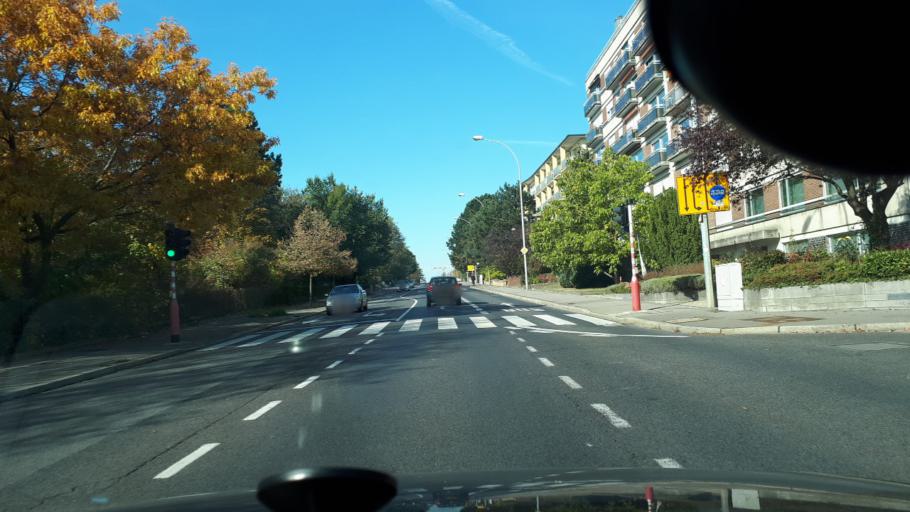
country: LU
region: Luxembourg
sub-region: Canton de Luxembourg
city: Luxembourg
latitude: 49.6151
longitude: 6.1078
